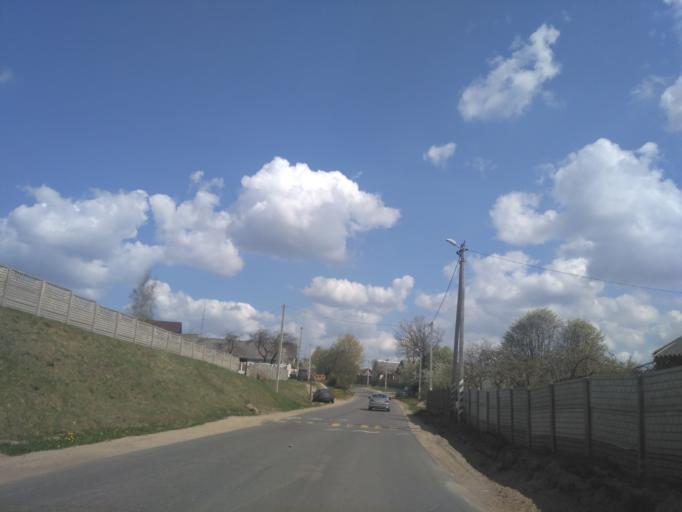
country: BY
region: Minsk
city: Radashkovichy
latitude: 54.1596
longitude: 27.2434
